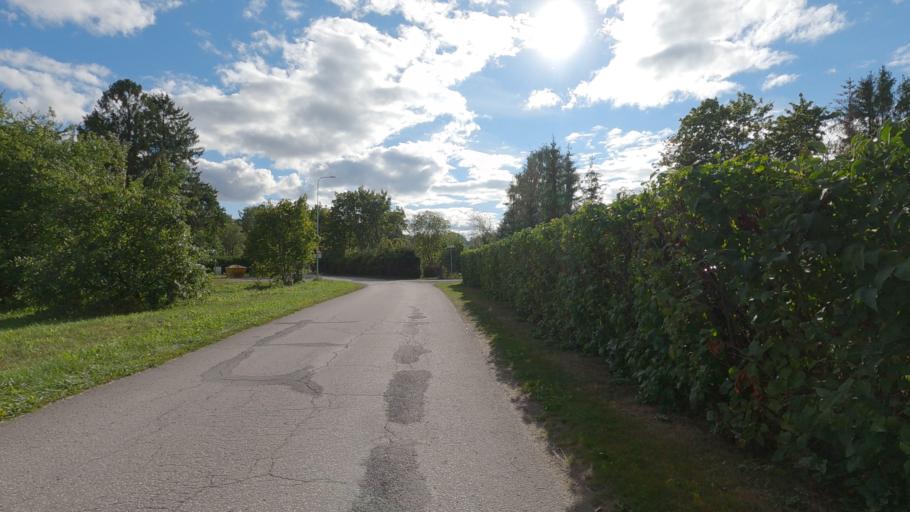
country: EE
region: Raplamaa
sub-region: Rapla vald
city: Rapla
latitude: 59.0050
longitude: 24.8041
